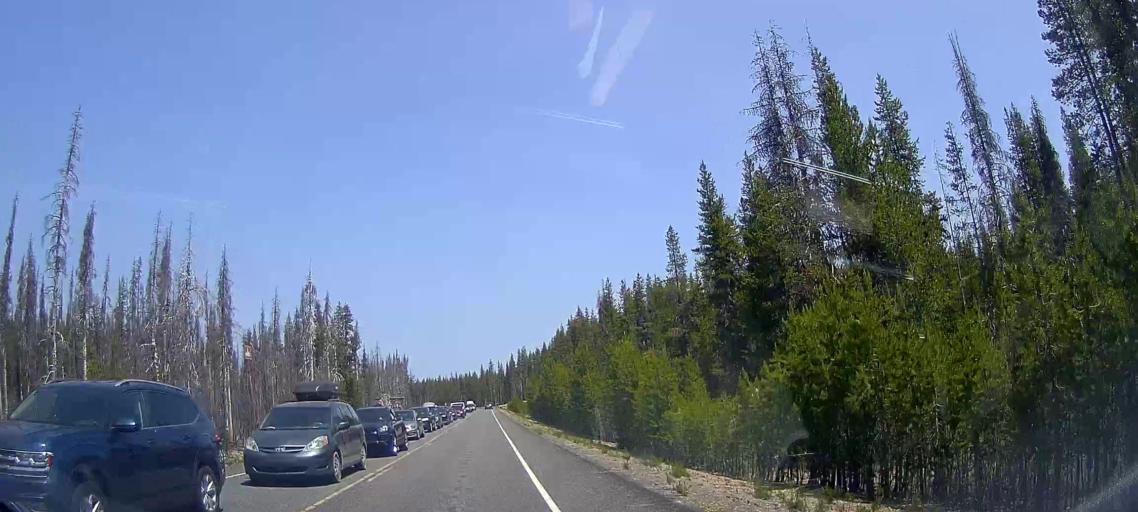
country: US
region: Oregon
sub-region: Lane County
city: Oakridge
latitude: 43.0849
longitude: -122.1166
